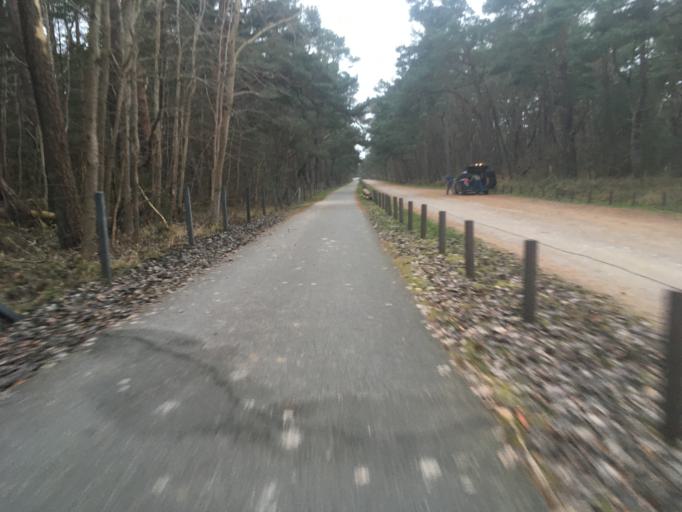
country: DE
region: Mecklenburg-Vorpommern
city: Sagard
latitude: 54.4700
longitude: 13.5681
